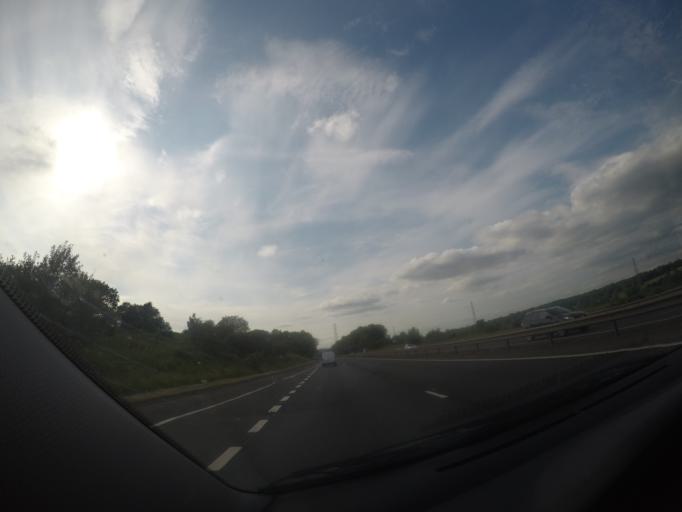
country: GB
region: Scotland
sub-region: South Lanarkshire
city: Larkhall
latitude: 55.7604
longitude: -3.9801
